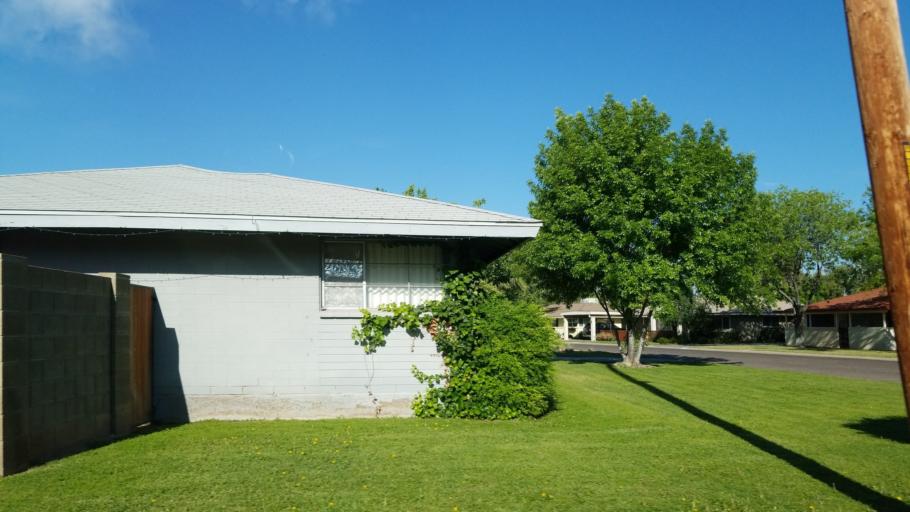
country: US
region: Arizona
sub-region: Maricopa County
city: Phoenix
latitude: 33.5151
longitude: -112.0869
